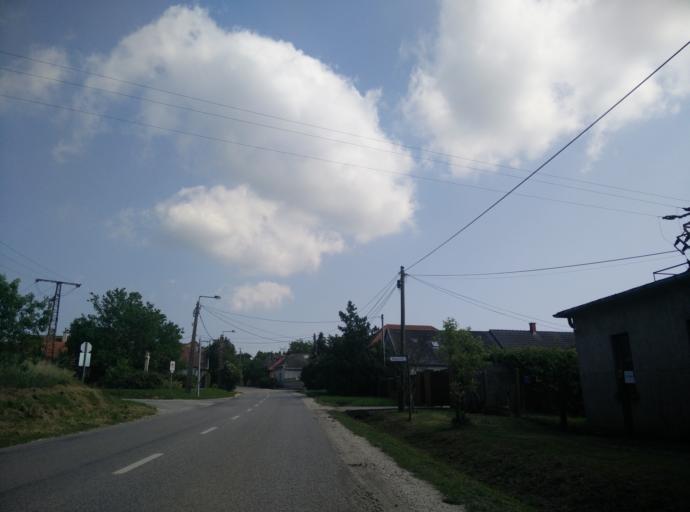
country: HU
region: Pest
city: Biatorbagy
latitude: 47.4698
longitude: 18.8034
